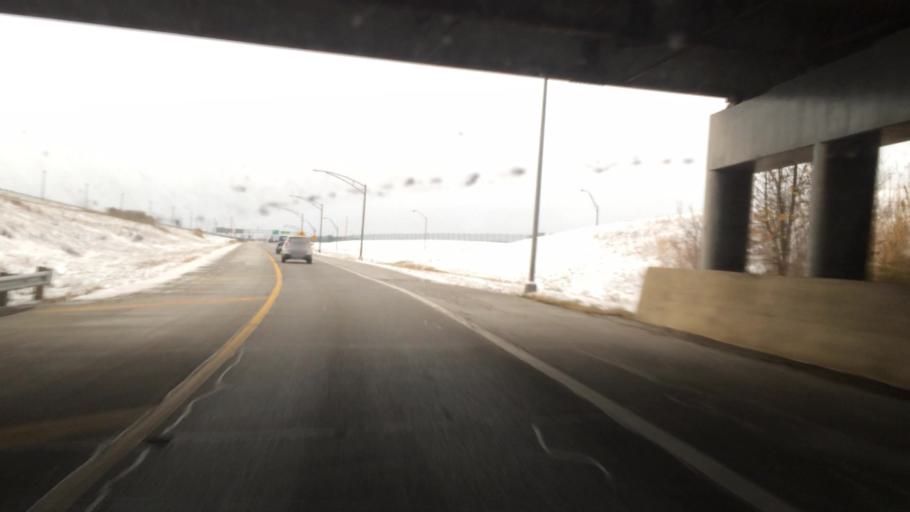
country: US
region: Ohio
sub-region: Cuyahoga County
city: Brook Park
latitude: 41.4187
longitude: -81.8300
